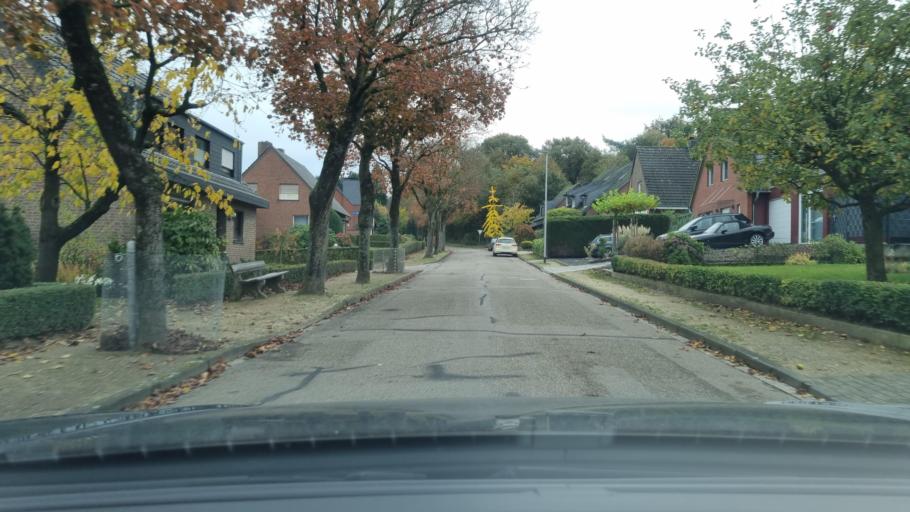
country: DE
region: North Rhine-Westphalia
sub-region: Regierungsbezirk Dusseldorf
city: Kleve
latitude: 51.7964
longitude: 6.0888
